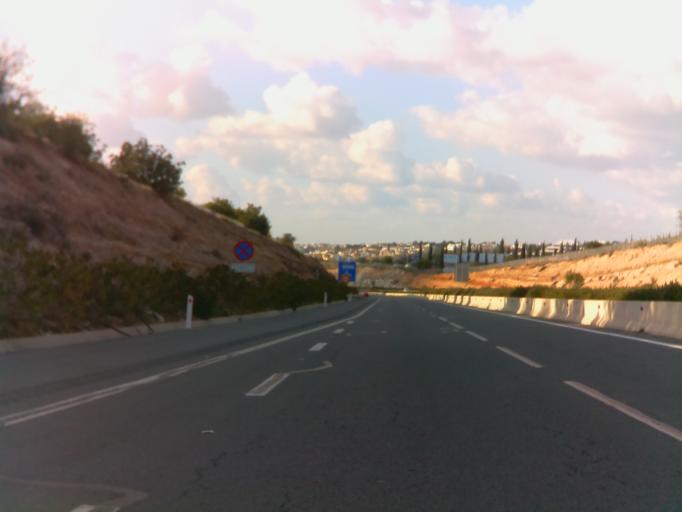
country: CY
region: Pafos
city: Paphos
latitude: 34.7797
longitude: 32.4547
